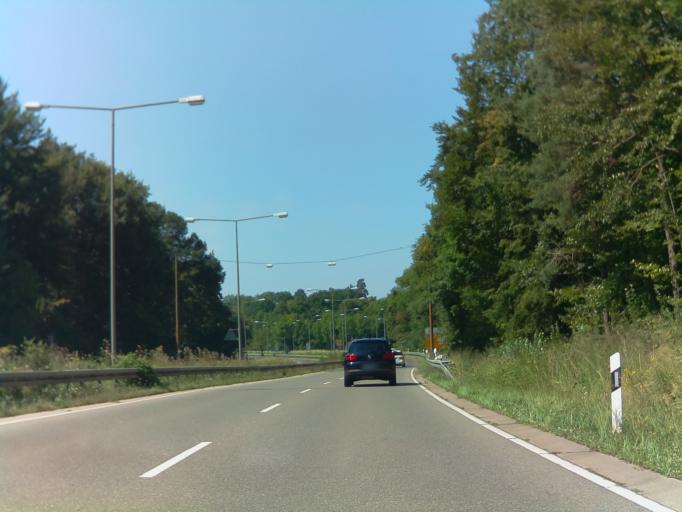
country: DE
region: Baden-Wuerttemberg
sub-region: Regierungsbezirk Stuttgart
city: Gerlingen
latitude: 48.7855
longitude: 9.0715
